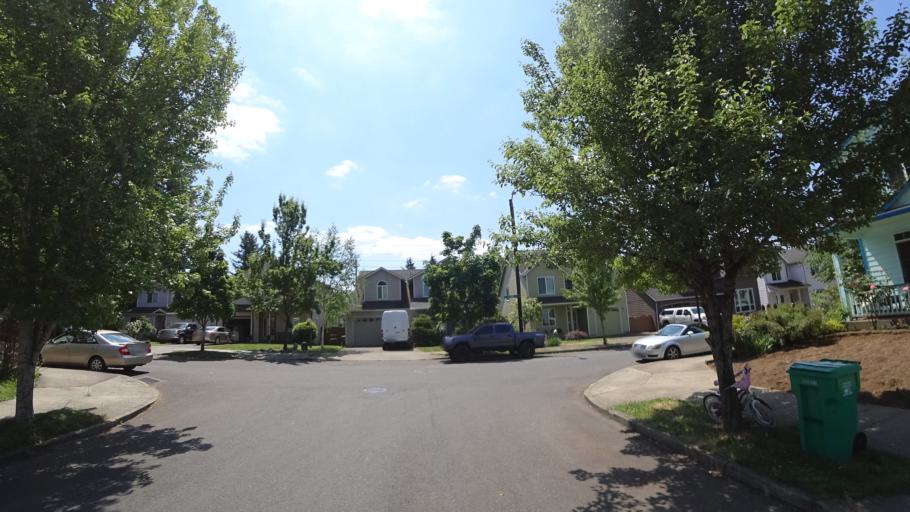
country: US
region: Oregon
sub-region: Clackamas County
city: Happy Valley
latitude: 45.4818
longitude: -122.5227
